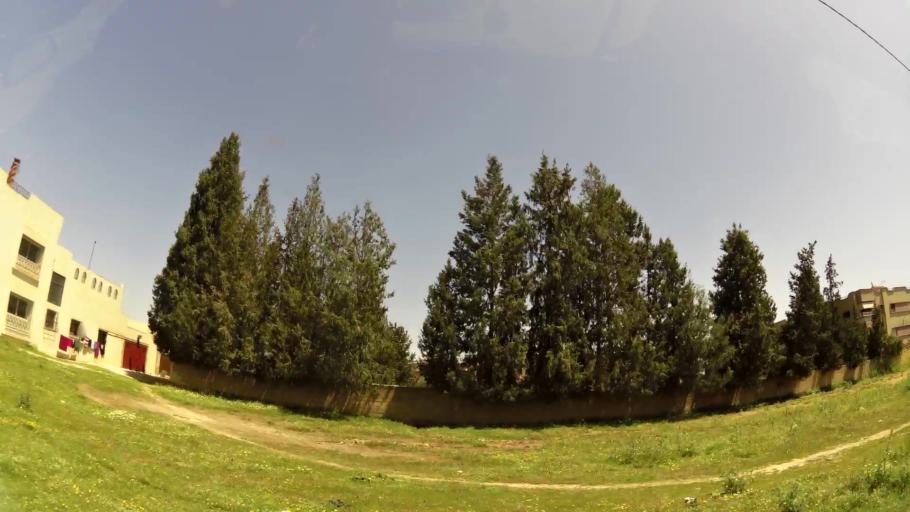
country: MA
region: Rabat-Sale-Zemmour-Zaer
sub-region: Khemisset
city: Khemisset
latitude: 33.8133
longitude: -6.0771
